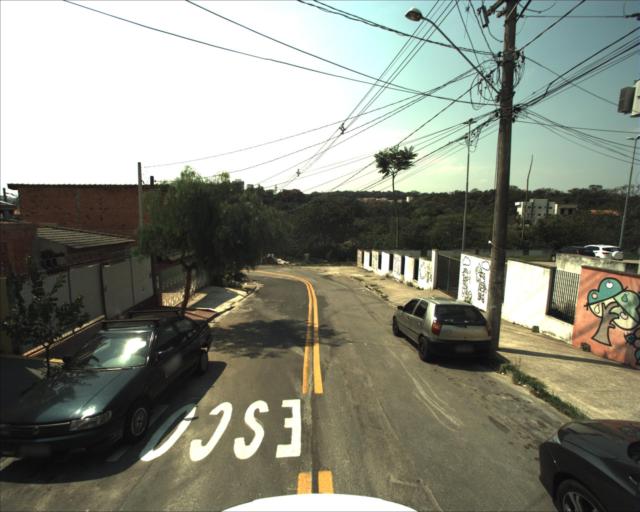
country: BR
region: Sao Paulo
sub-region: Sorocaba
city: Sorocaba
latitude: -23.4444
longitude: -47.4858
